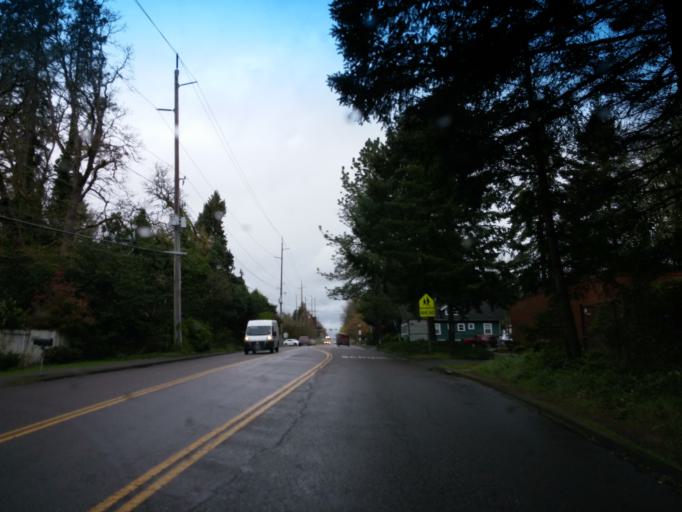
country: US
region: Oregon
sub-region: Washington County
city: Aloha
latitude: 45.5023
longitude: -122.8518
